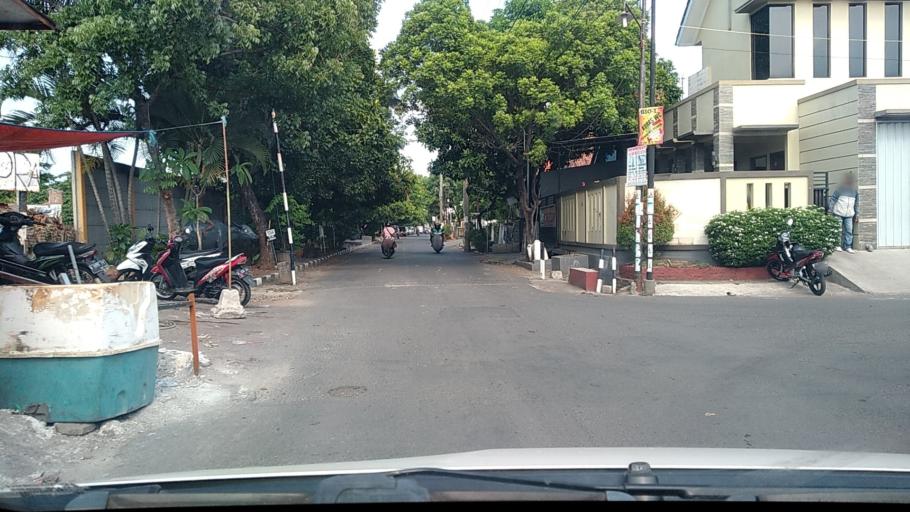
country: ID
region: Central Java
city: Semarang
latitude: -6.9781
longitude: 110.3968
